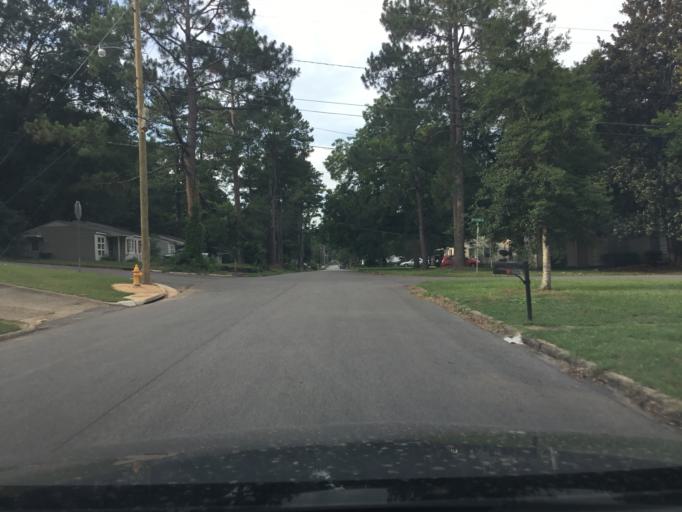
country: US
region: Alabama
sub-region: Montgomery County
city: Montgomery
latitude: 32.3652
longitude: -86.2469
